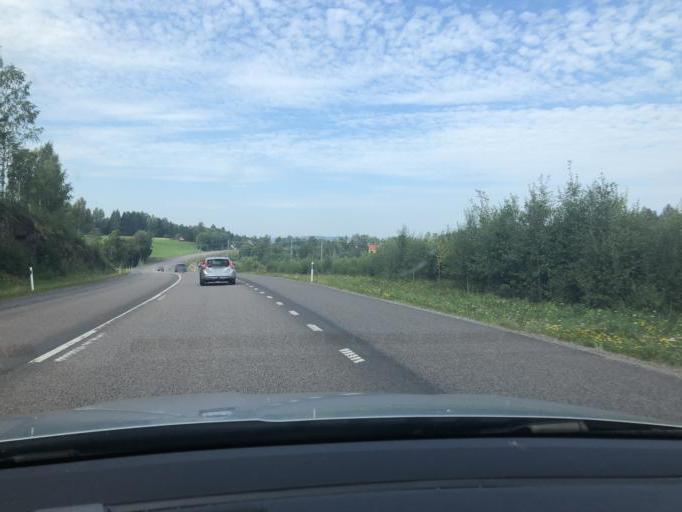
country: SE
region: Vaesternorrland
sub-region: Kramfors Kommun
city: Kramfors
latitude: 62.8993
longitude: 17.8430
